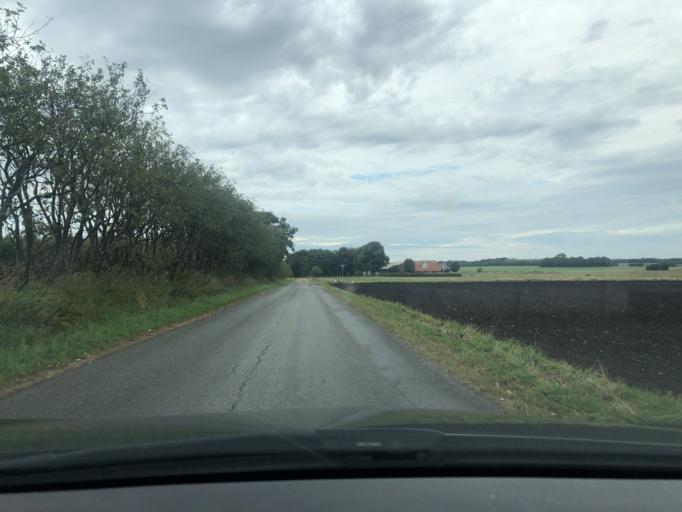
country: DK
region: South Denmark
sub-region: Varde Kommune
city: Olgod
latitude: 55.7966
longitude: 8.6913
